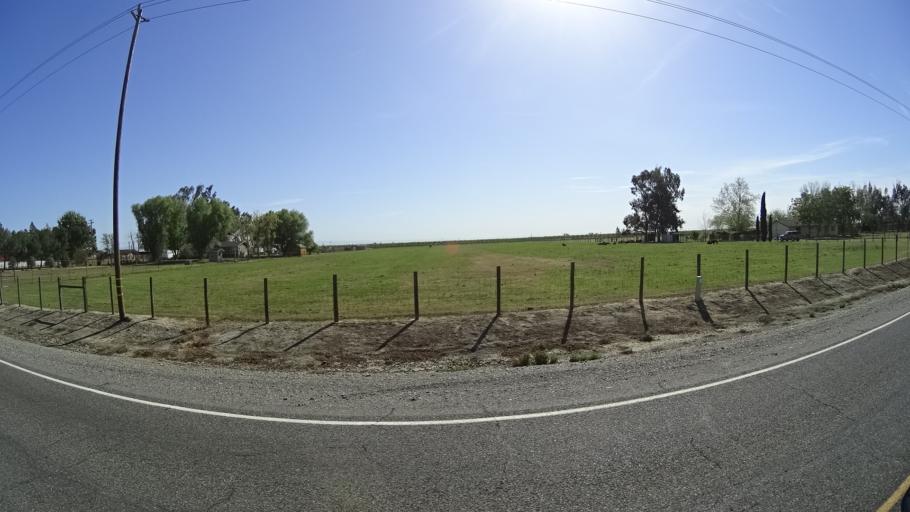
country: US
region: California
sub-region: Glenn County
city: Orland
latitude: 39.6369
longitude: -122.1974
